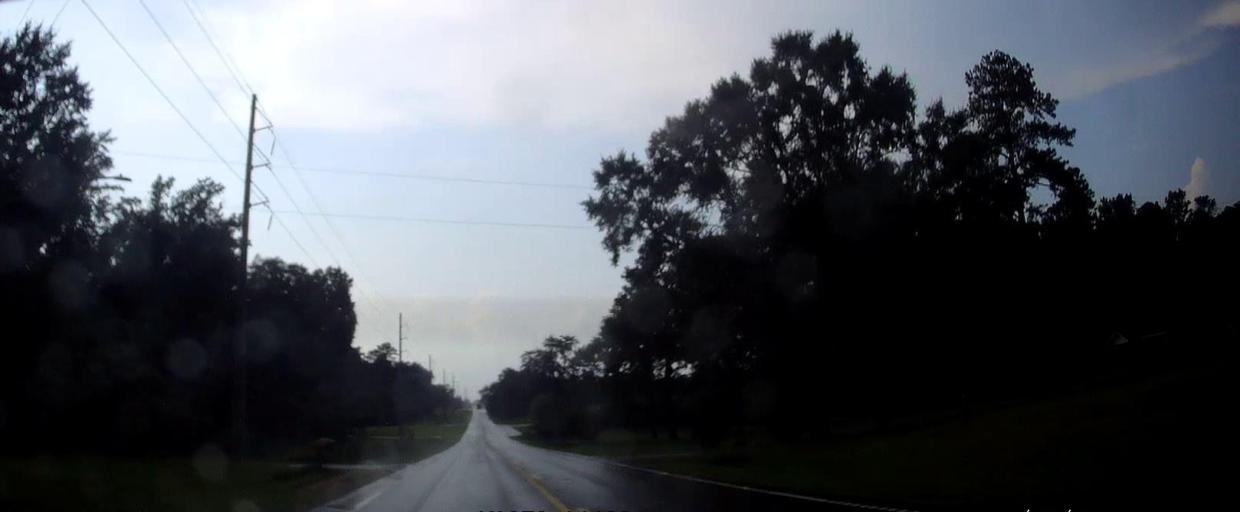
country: US
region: Georgia
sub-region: Twiggs County
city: Jeffersonville
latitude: 32.5865
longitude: -83.2228
